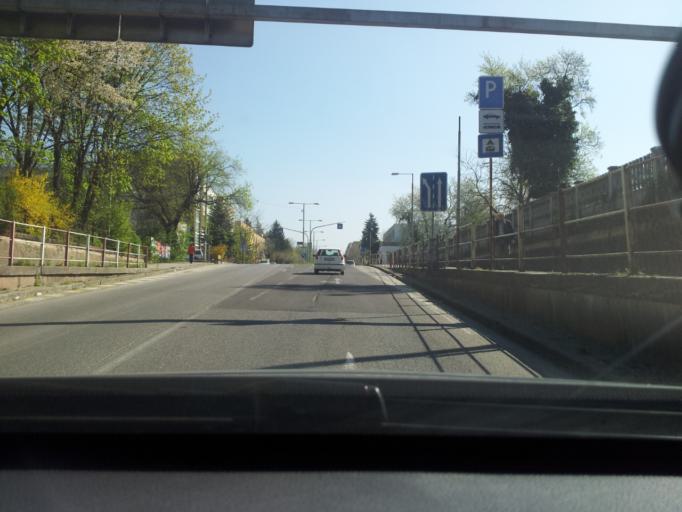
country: SK
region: Trenciansky
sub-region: Okres Trencin
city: Trencin
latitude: 48.8972
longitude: 18.0469
